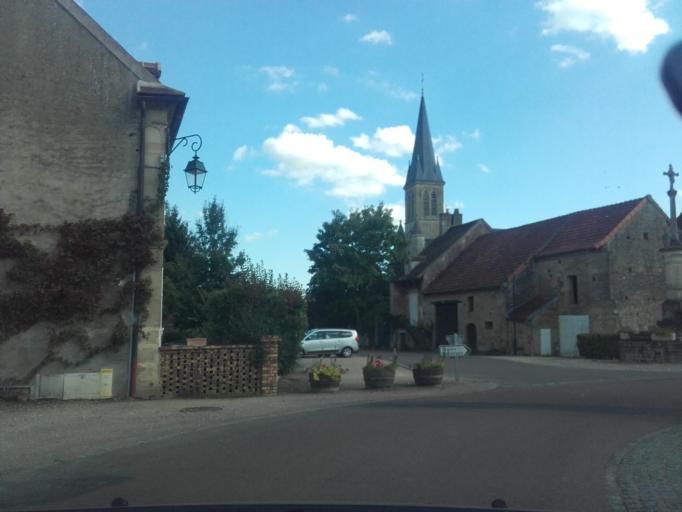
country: FR
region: Bourgogne
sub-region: Departement de Saone-et-Loire
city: Epinac
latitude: 47.0091
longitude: 4.4715
